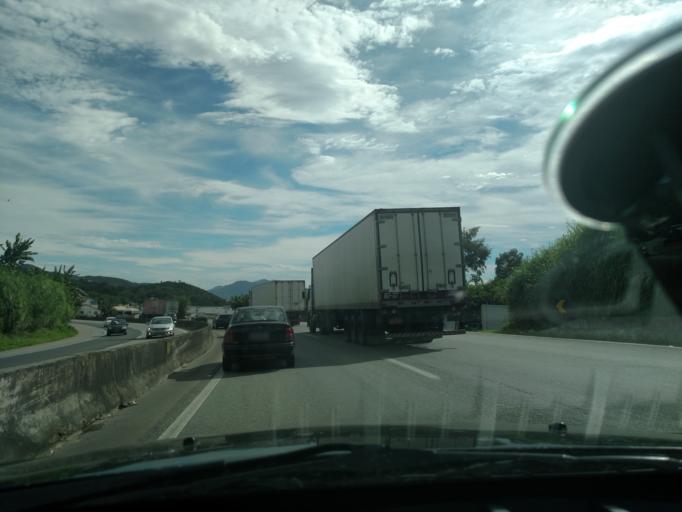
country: BR
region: Santa Catarina
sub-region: Biguacu
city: Biguacu
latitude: -27.4775
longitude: -48.6414
